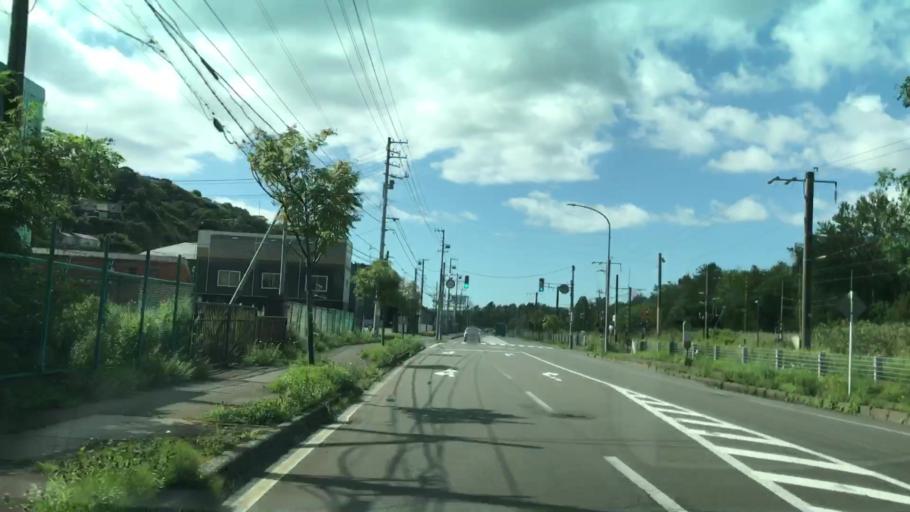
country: JP
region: Hokkaido
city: Muroran
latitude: 42.3339
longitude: 141.0012
